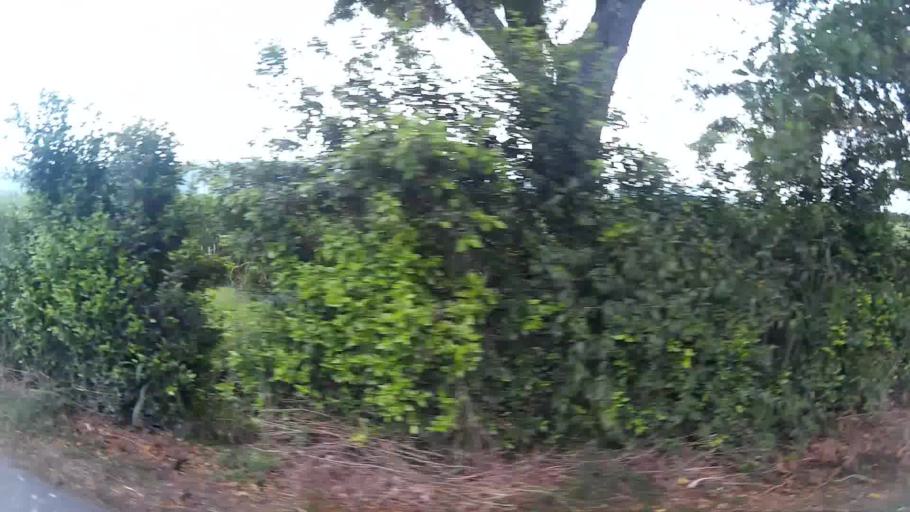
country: CO
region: Risaralda
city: La Virginia
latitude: 4.9086
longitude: -75.8759
